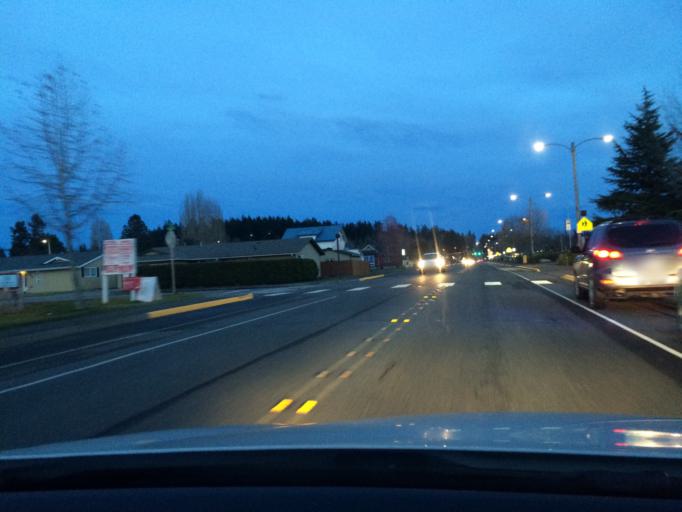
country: US
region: Washington
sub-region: Whatcom County
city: Blaine
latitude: 48.9940
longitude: -122.7406
